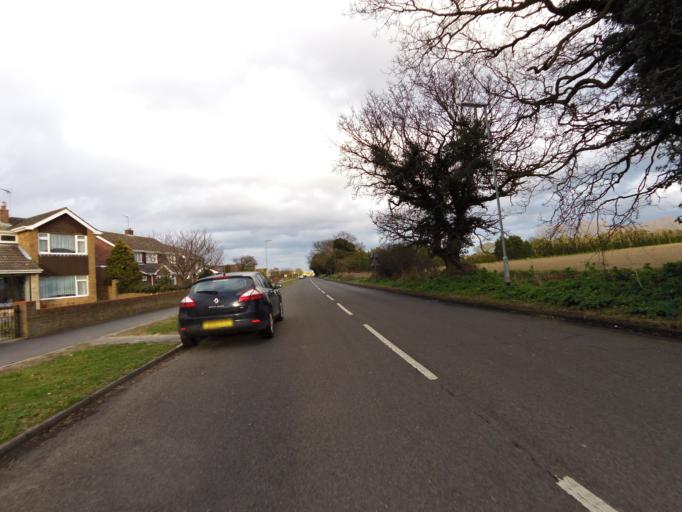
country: GB
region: England
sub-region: Norfolk
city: Gorleston-on-Sea
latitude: 52.5562
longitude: 1.7187
